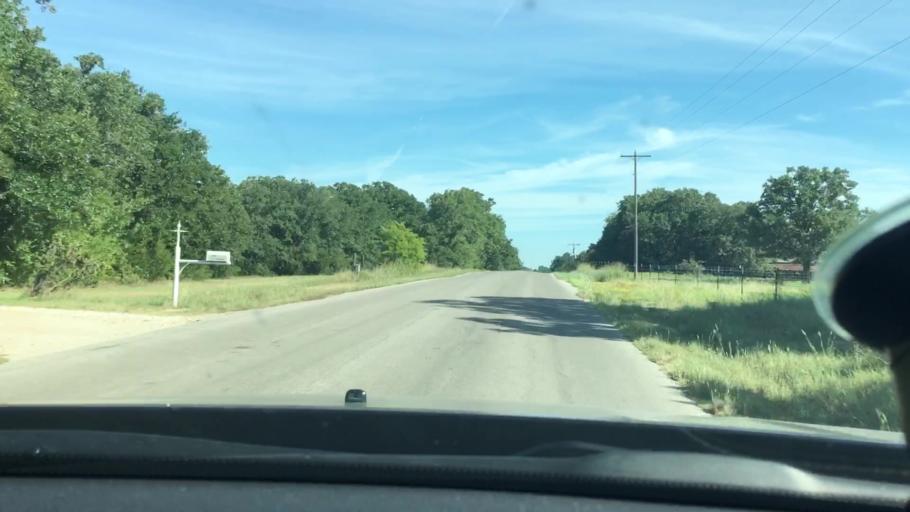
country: US
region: Oklahoma
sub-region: Carter County
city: Lone Grove
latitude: 34.2358
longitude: -97.2474
